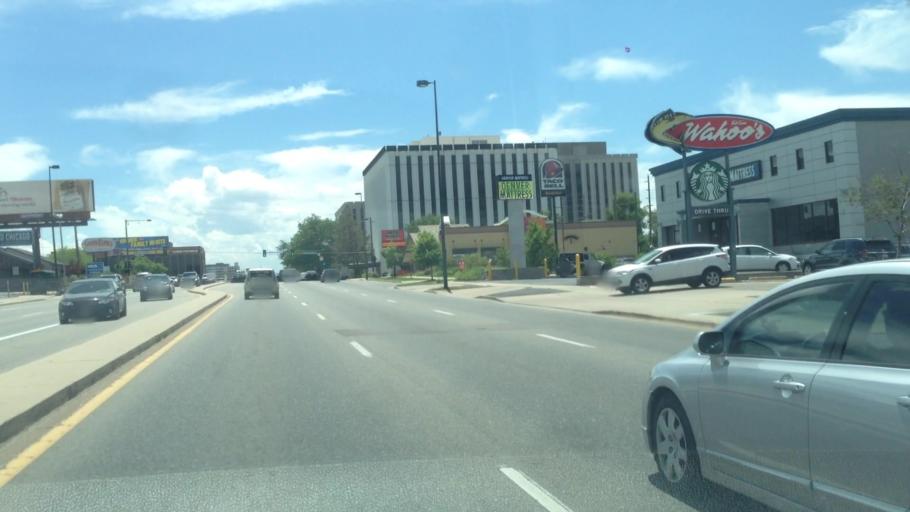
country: US
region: Colorado
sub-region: Arapahoe County
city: Glendale
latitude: 39.6945
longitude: -104.9407
